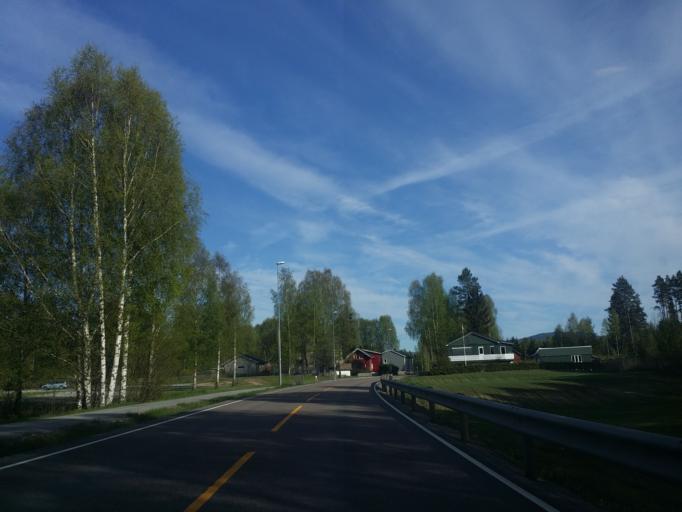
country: NO
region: Telemark
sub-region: Notodden
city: Notodden
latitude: 59.5916
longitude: 9.1510
